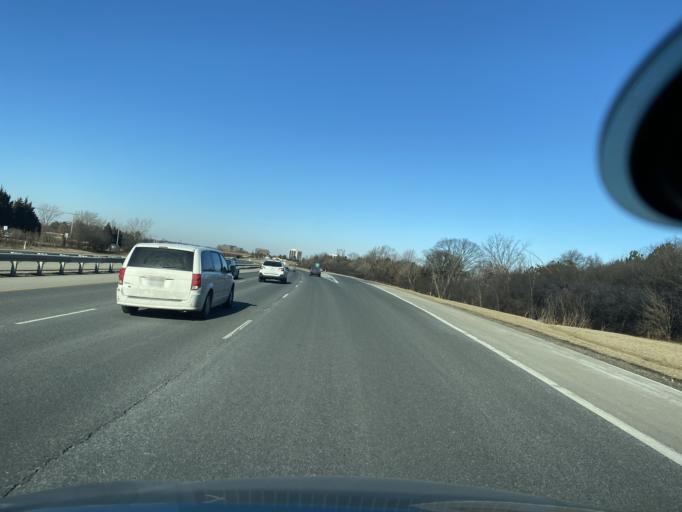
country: US
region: Illinois
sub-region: DuPage County
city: Oak Brook
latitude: 41.8270
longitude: -87.9534
